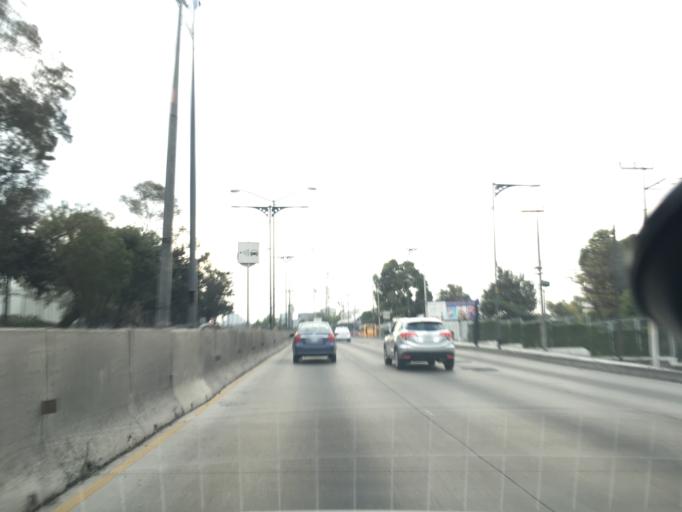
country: MX
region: Mexico City
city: Col. Bosques de las Lomas
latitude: 19.3804
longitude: -99.2558
